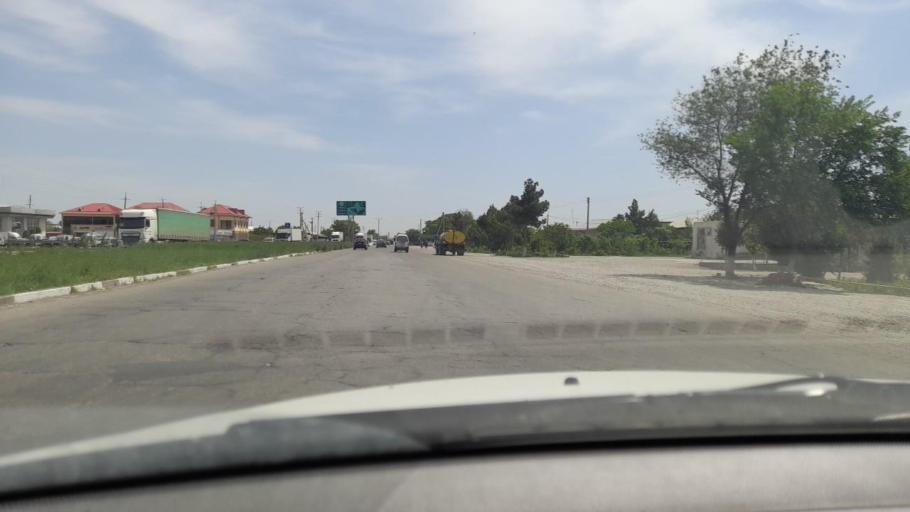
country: UZ
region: Bukhara
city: Ghijduwon
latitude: 40.0867
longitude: 64.6726
